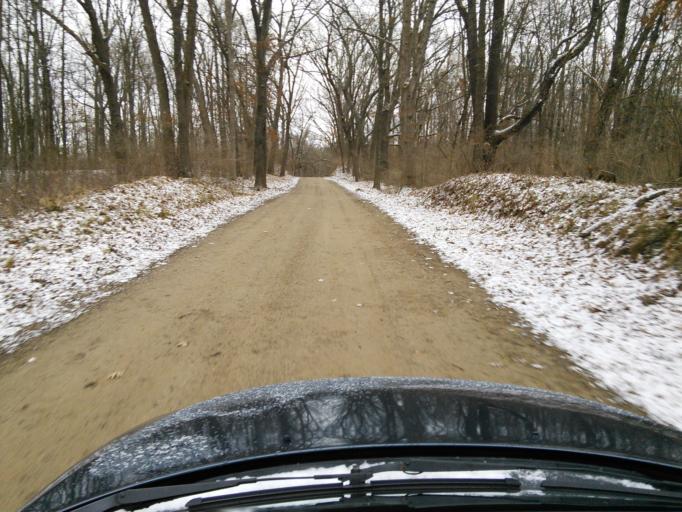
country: US
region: Michigan
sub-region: Jackson County
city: Grass Lake
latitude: 42.3107
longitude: -84.1849
